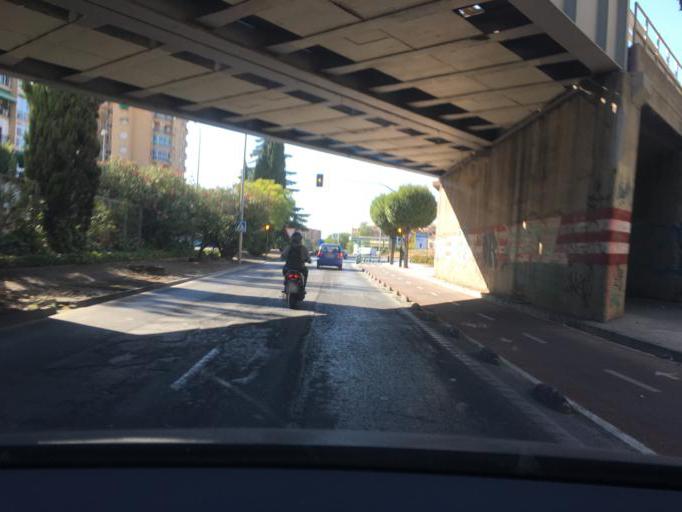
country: ES
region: Andalusia
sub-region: Provincia de Granada
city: Granada
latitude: 37.1914
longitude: -3.6187
